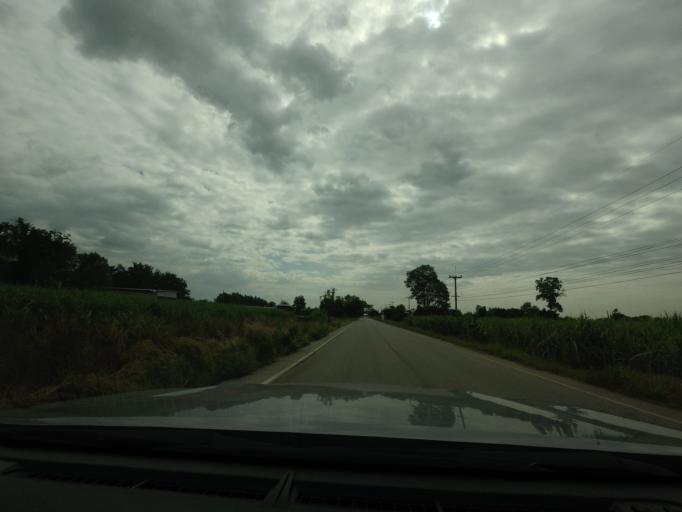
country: TH
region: Phitsanulok
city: Noen Maprang
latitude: 16.6540
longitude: 100.6159
